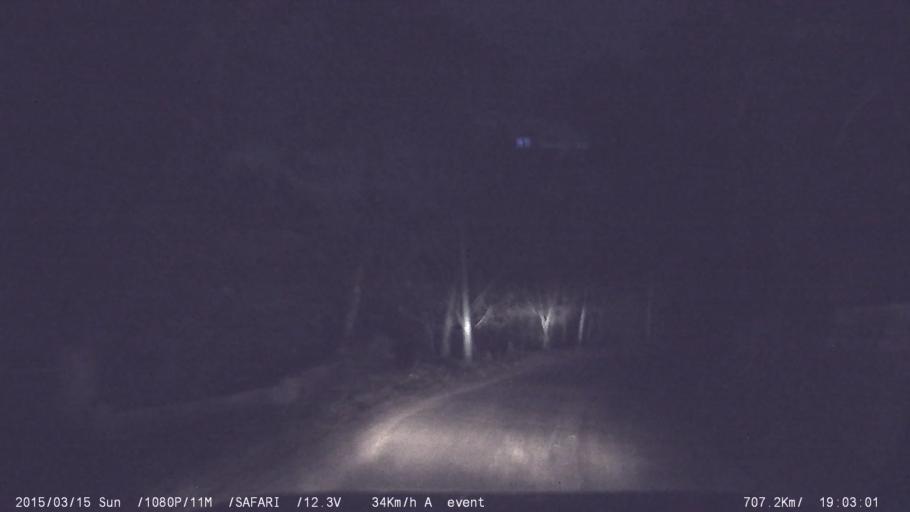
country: IN
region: Kerala
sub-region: Ernakulam
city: Muvattupuzha
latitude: 9.8791
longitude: 76.6469
